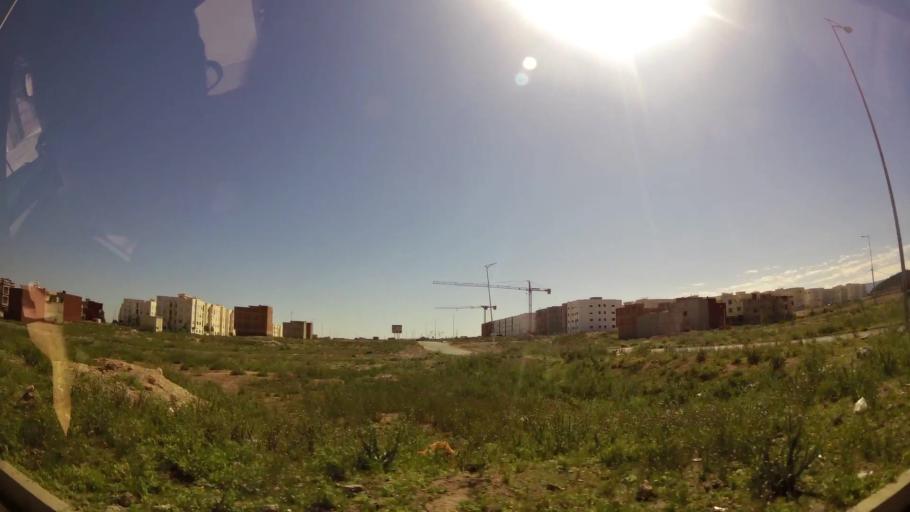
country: MA
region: Oriental
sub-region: Oujda-Angad
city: Oujda
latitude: 34.6539
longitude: -1.8846
